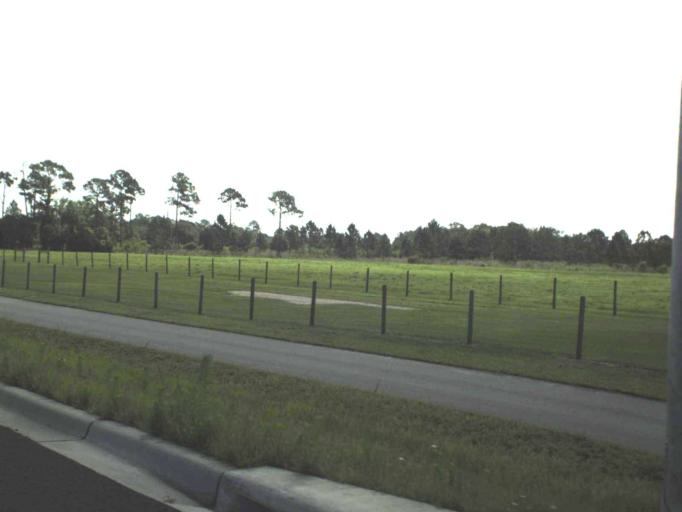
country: US
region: Florida
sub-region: Seminole County
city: Midway
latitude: 28.8290
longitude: -81.1774
